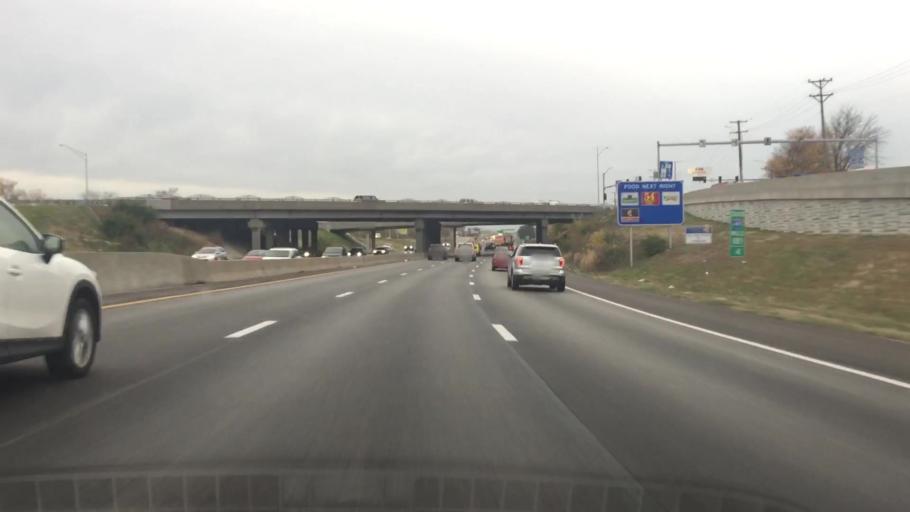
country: US
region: Missouri
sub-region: Jackson County
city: Grandview
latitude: 38.9093
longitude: -94.5239
